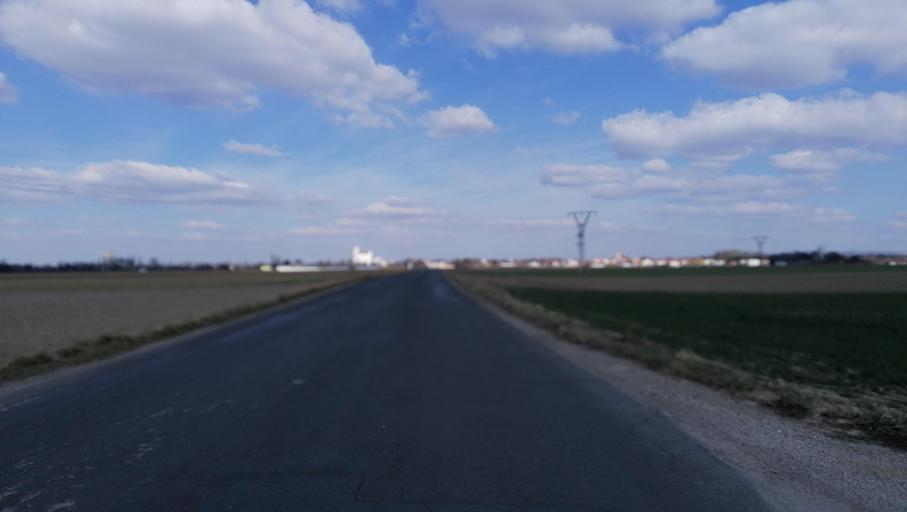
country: AT
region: Lower Austria
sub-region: Politischer Bezirk Wiener Neustadt
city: Lichtenworth
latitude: 47.8243
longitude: 16.2785
